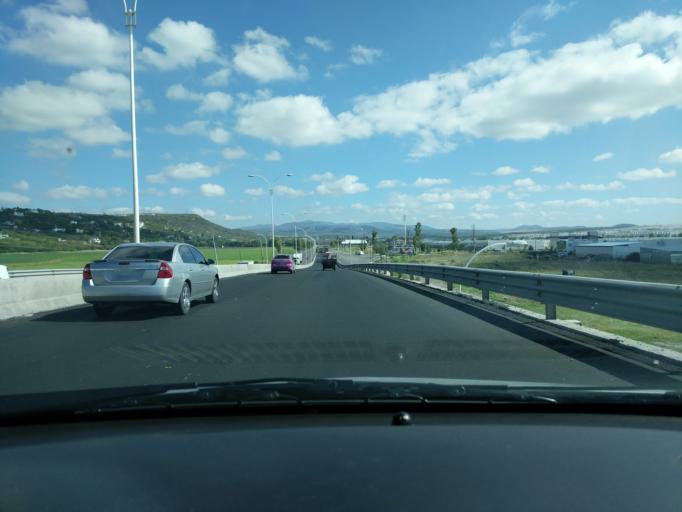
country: MX
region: Queretaro
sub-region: Queretaro
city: Patria Nueva
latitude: 20.6223
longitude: -100.4963
